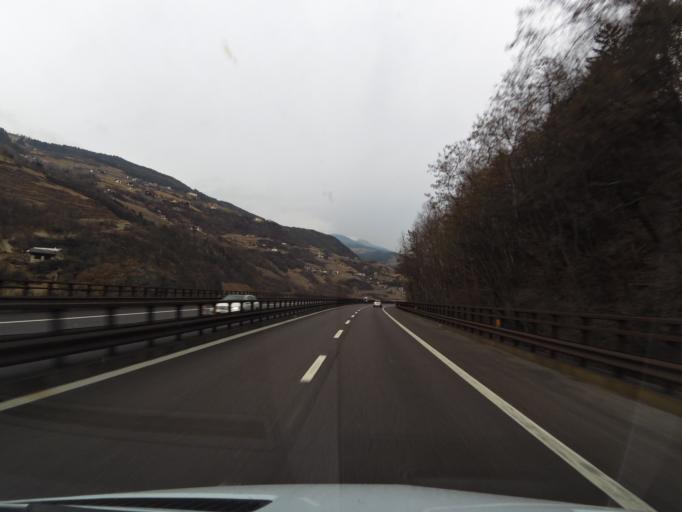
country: IT
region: Trentino-Alto Adige
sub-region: Bolzano
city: Villandro
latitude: 46.6272
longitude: 11.5507
